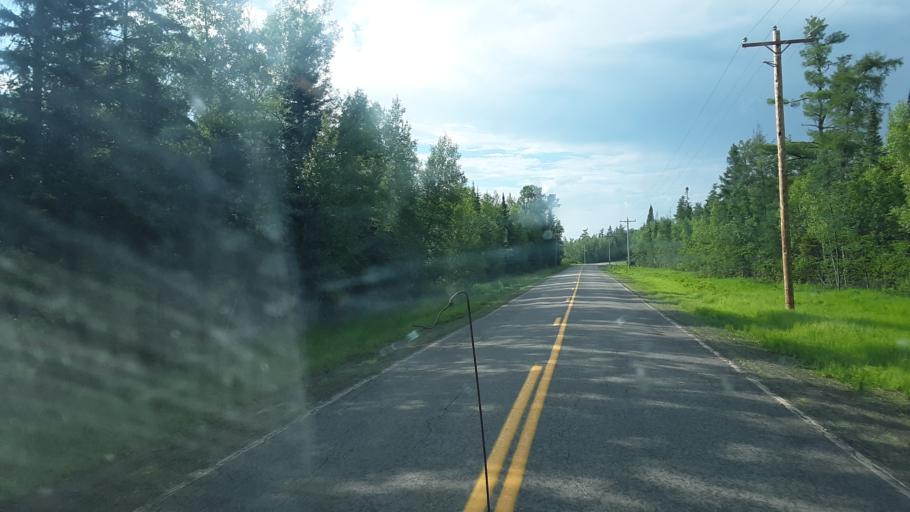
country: US
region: Maine
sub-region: Washington County
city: Calais
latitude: 45.1820
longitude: -67.5174
